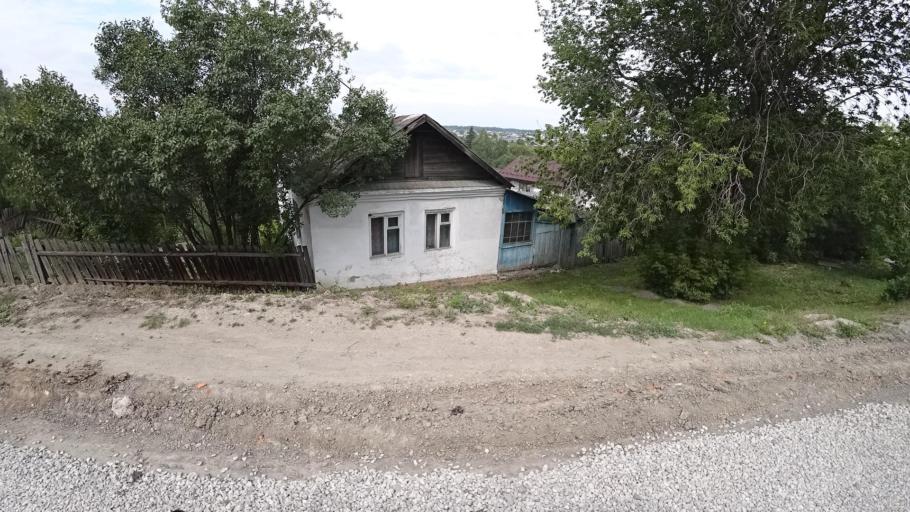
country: RU
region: Sverdlovsk
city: Kamyshlov
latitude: 56.8528
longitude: 62.7097
